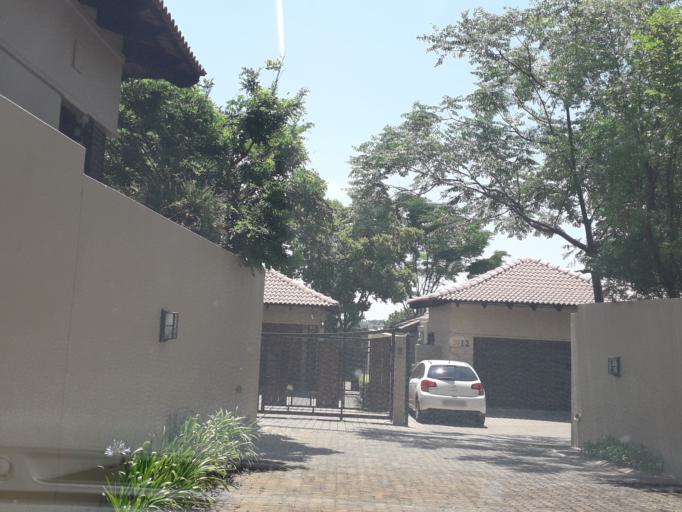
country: ZA
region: Gauteng
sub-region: City of Johannesburg Metropolitan Municipality
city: Diepsloot
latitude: -26.0664
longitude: 28.0171
